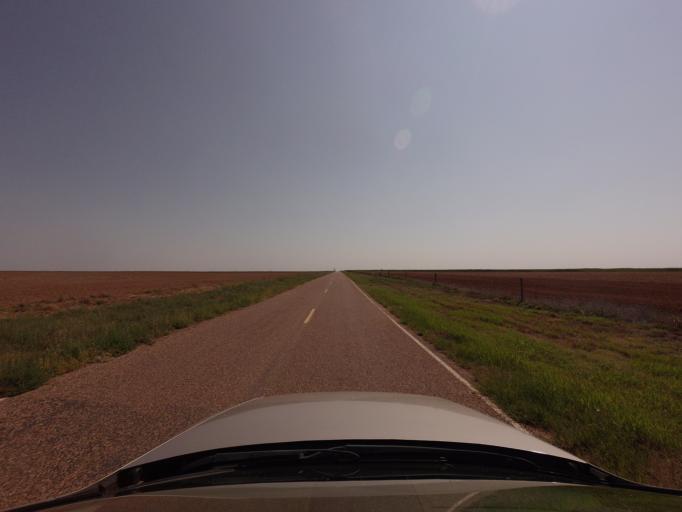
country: US
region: New Mexico
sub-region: Curry County
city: Cannon Air Force Base
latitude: 34.6329
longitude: -103.3571
